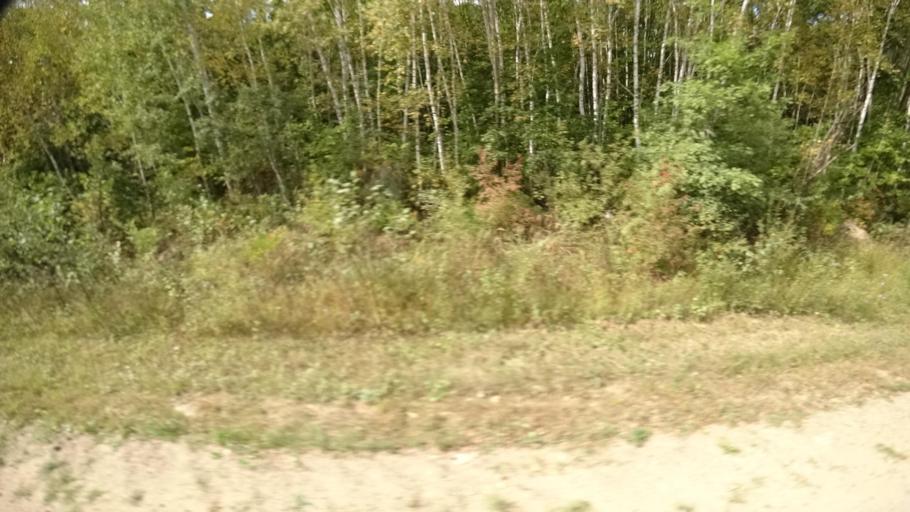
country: RU
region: Primorskiy
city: Yakovlevka
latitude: 44.6744
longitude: 133.6121
